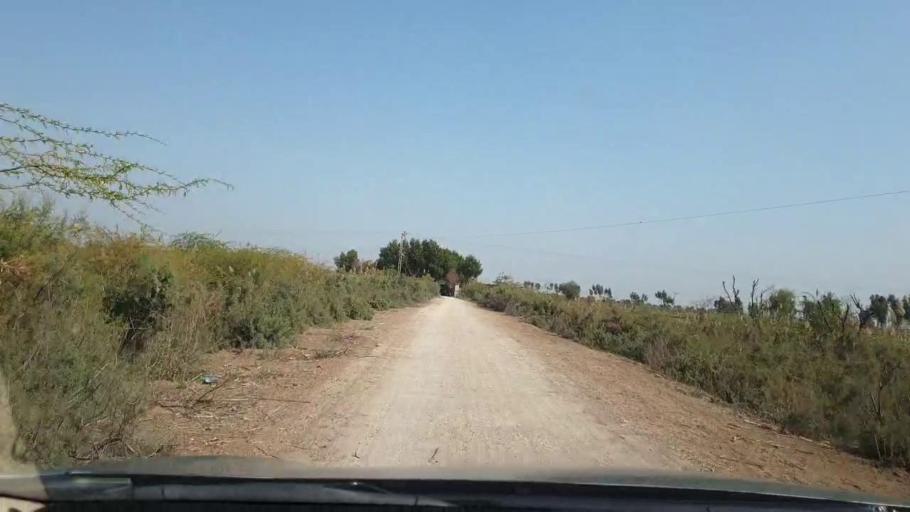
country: PK
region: Sindh
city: Mirpur Khas
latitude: 25.6119
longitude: 68.8914
